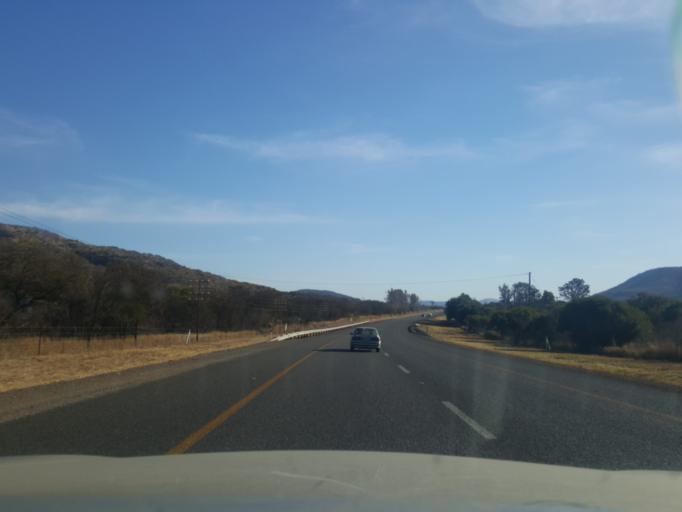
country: ZA
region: North-West
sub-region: Ngaka Modiri Molema District Municipality
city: Zeerust
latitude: -25.5292
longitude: 26.1464
